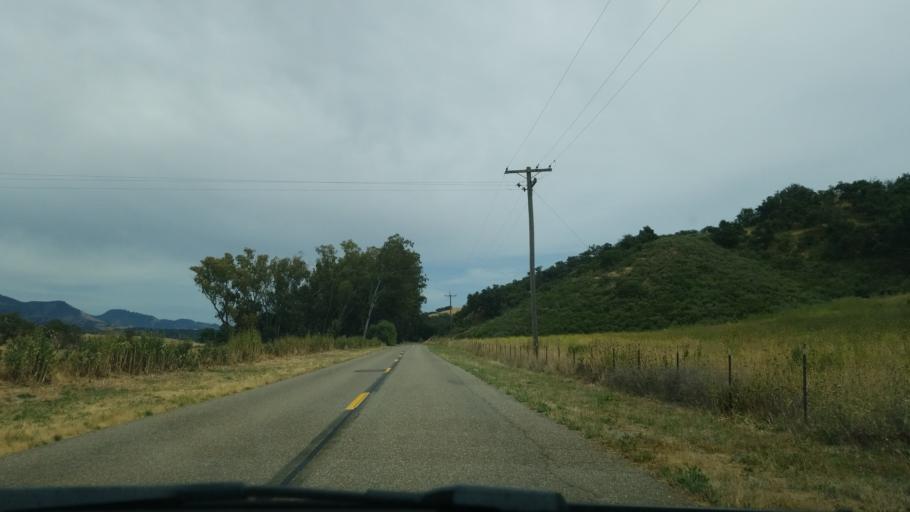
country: US
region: California
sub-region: Santa Barbara County
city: Los Alamos
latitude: 34.7816
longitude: -120.1619
